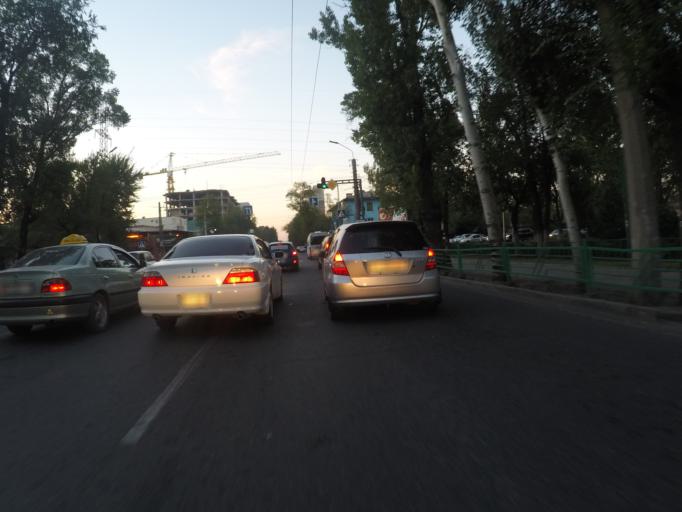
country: KG
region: Chuy
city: Bishkek
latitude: 42.8518
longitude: 74.6098
